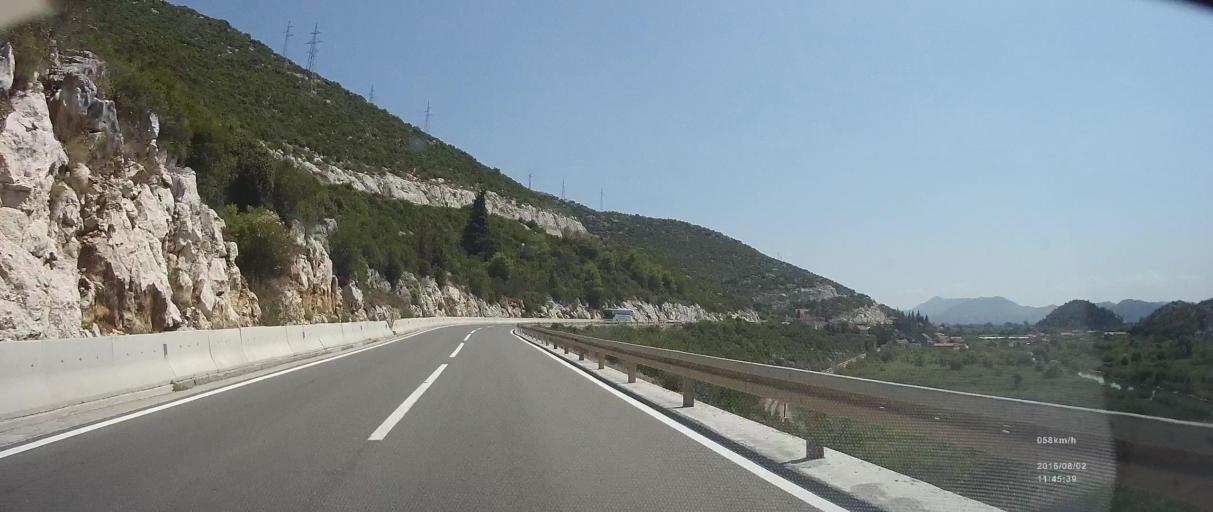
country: HR
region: Dubrovacko-Neretvanska
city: Komin
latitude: 43.0541
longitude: 17.4673
